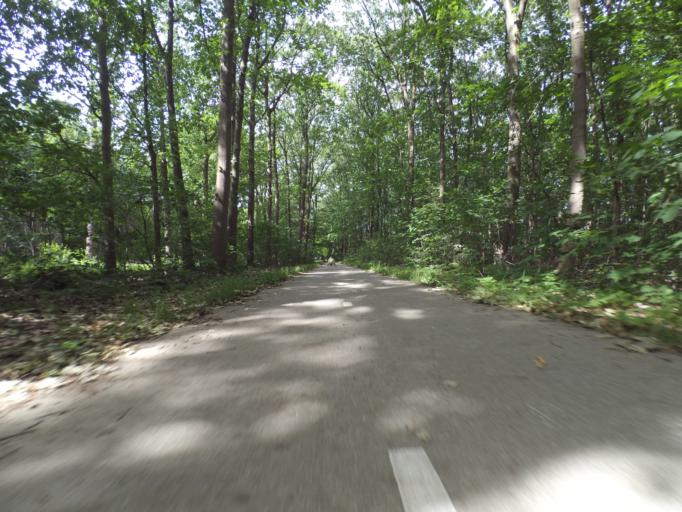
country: BE
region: Flanders
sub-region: Provincie Antwerpen
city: Essen
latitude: 51.4667
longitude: 4.3855
